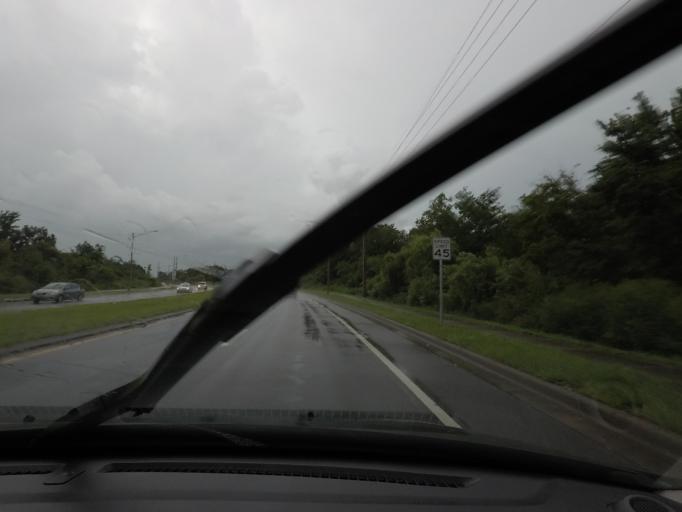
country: US
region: Florida
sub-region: Orange County
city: Belle Isle
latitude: 28.4553
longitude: -81.3310
